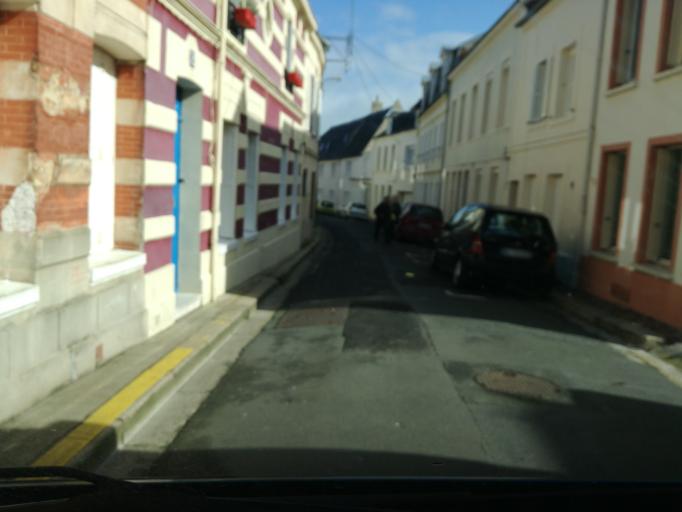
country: FR
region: Haute-Normandie
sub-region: Departement de la Seine-Maritime
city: Fecamp
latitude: 49.7554
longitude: 0.3756
